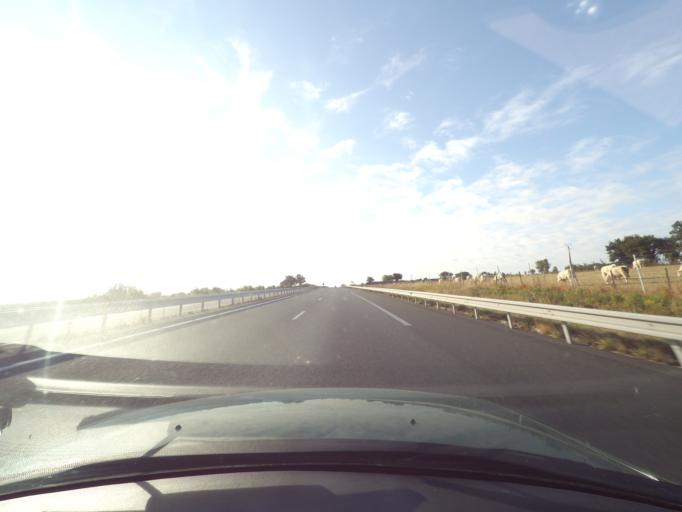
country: FR
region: Poitou-Charentes
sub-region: Departement des Deux-Sevres
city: Combrand
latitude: 46.9068
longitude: -0.6763
